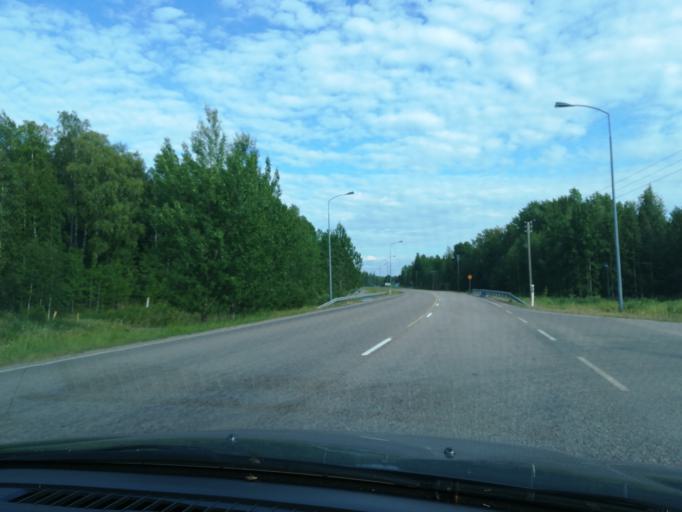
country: FI
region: South Karelia
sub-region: Imatra
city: Imatra
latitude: 61.1579
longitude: 28.7935
